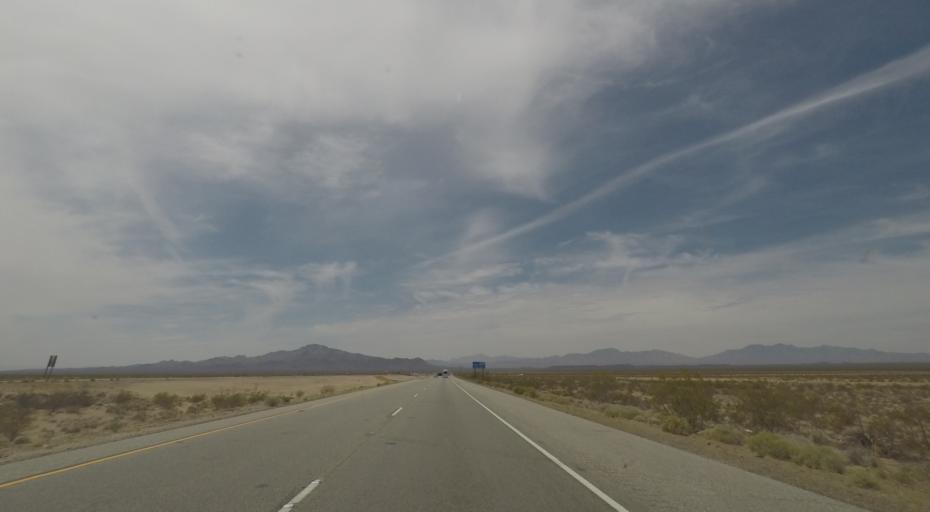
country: US
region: California
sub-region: San Bernardino County
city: Needles
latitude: 34.8110
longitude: -115.2033
